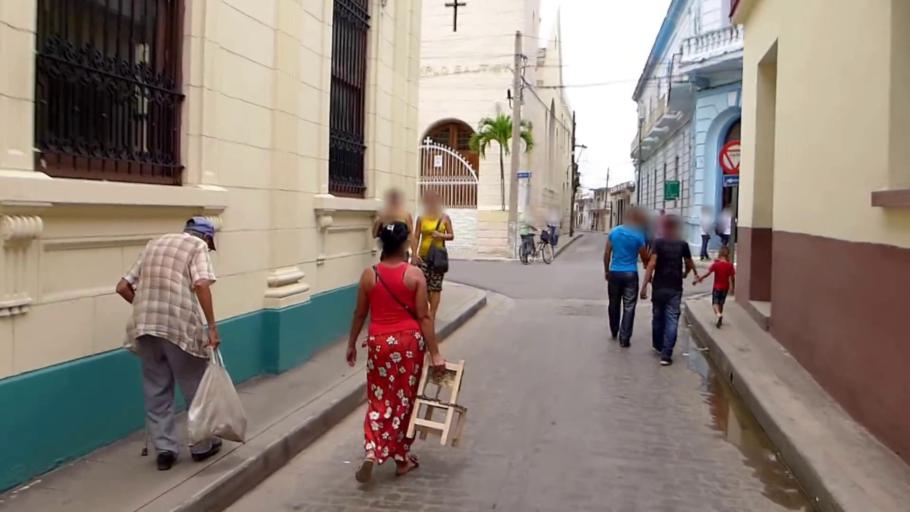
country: CU
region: Camaguey
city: Camaguey
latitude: 21.3803
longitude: -77.9191
